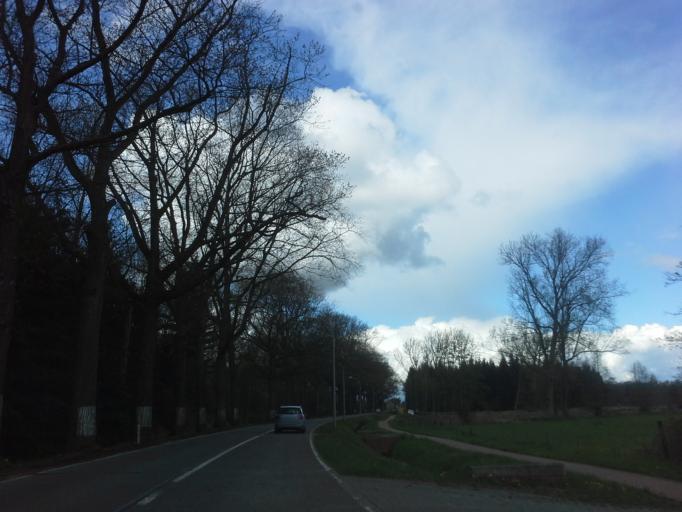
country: BE
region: Flanders
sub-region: Provincie Antwerpen
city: Meerhout
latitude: 51.1442
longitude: 5.0516
